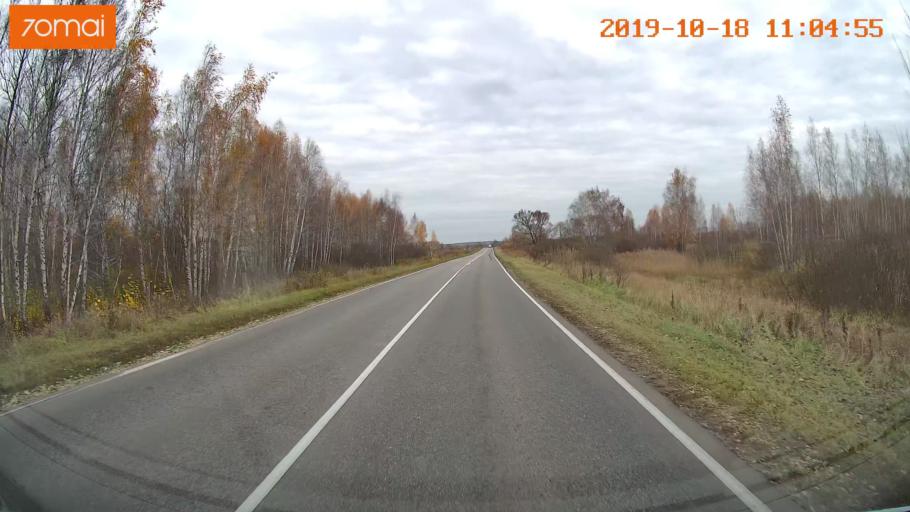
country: RU
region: Tula
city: Kimovsk
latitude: 53.8990
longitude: 38.5414
